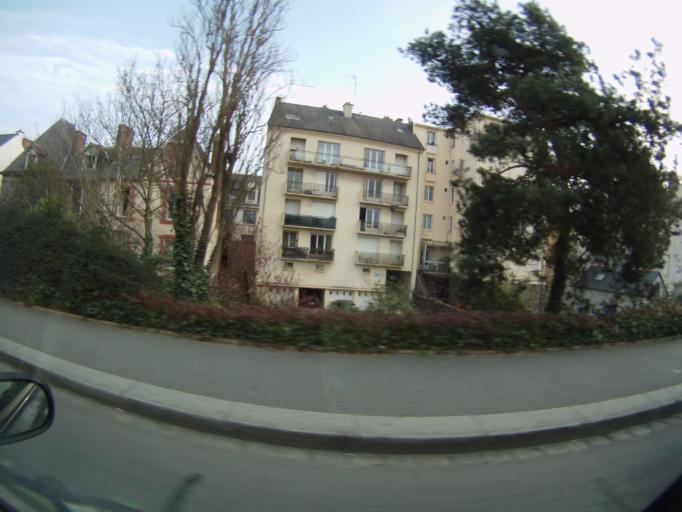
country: FR
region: Brittany
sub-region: Departement d'Ille-et-Vilaine
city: Rennes
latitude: 48.1050
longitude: -1.6649
